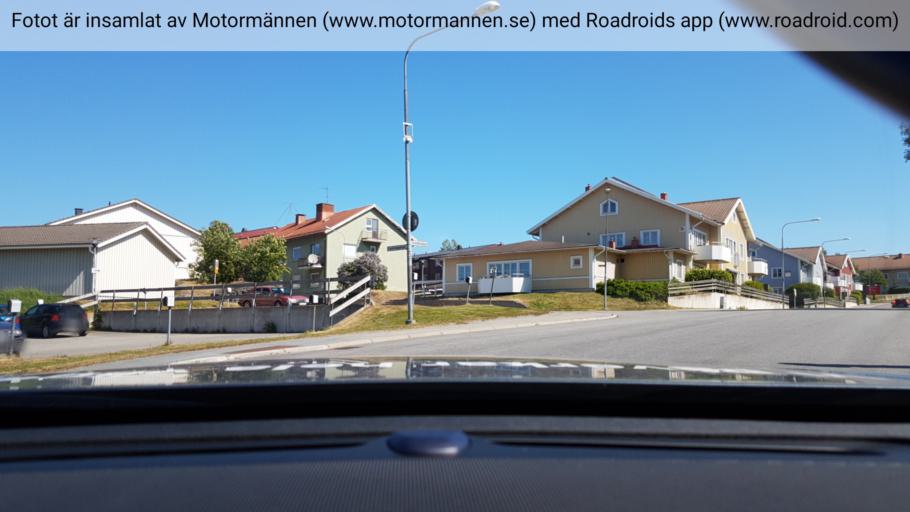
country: SE
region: Vaesterbotten
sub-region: Umea Kommun
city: Holmsund
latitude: 63.7094
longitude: 20.3634
